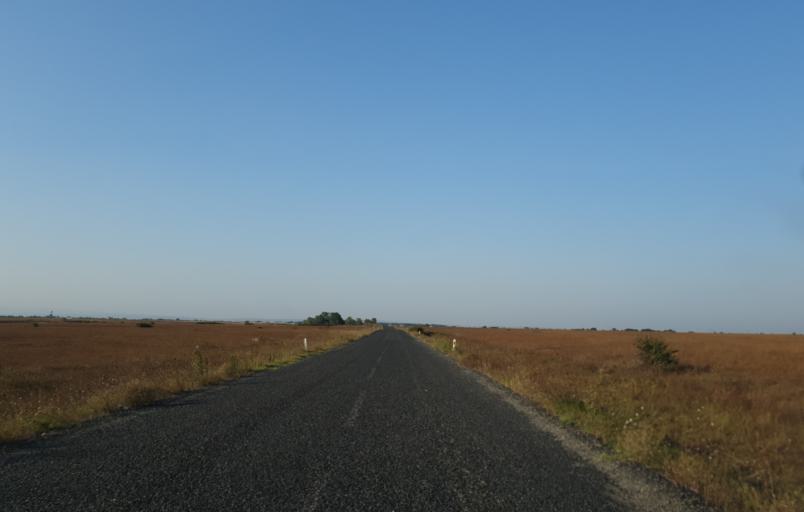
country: TR
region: Tekirdag
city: Beyazkoy
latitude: 41.4089
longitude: 27.7611
